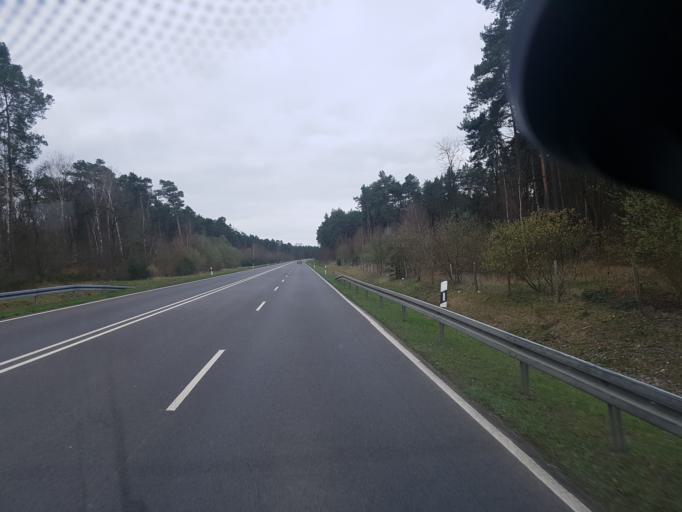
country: DE
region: Brandenburg
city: Beeskow
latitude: 52.1609
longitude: 14.2168
